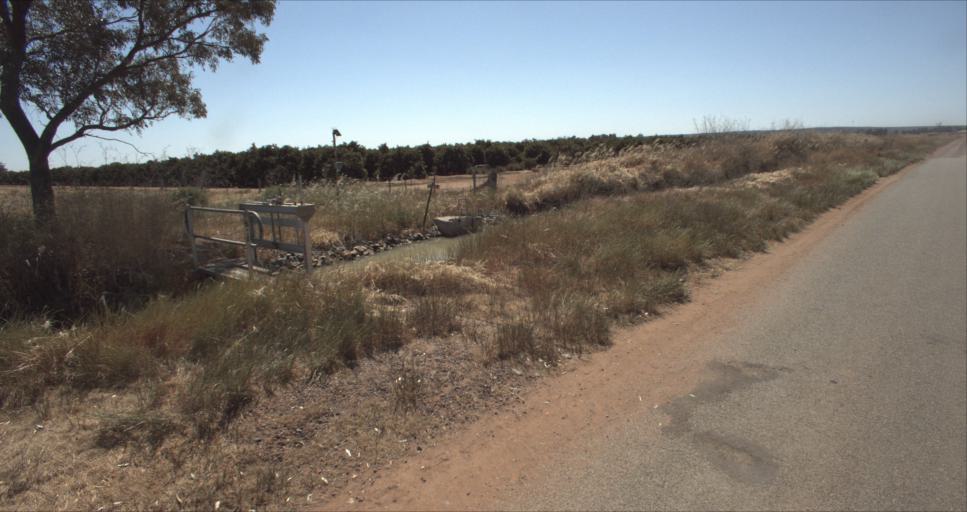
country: AU
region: New South Wales
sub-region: Leeton
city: Leeton
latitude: -34.4935
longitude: 146.4217
